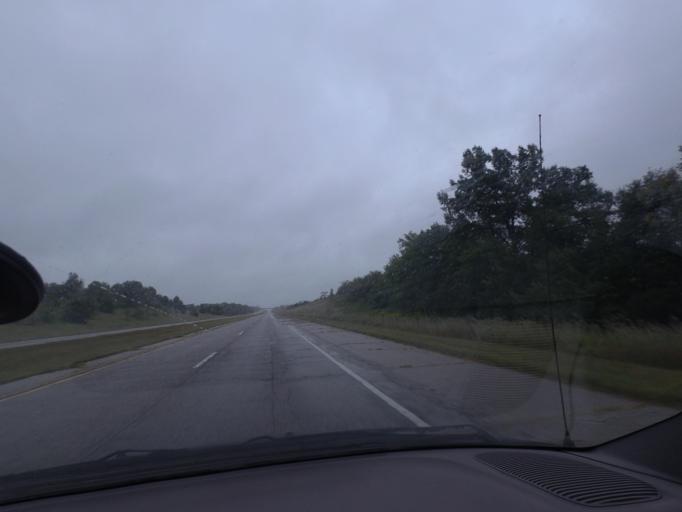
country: US
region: Illinois
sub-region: Pike County
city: Barry
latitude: 39.6907
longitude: -90.9282
